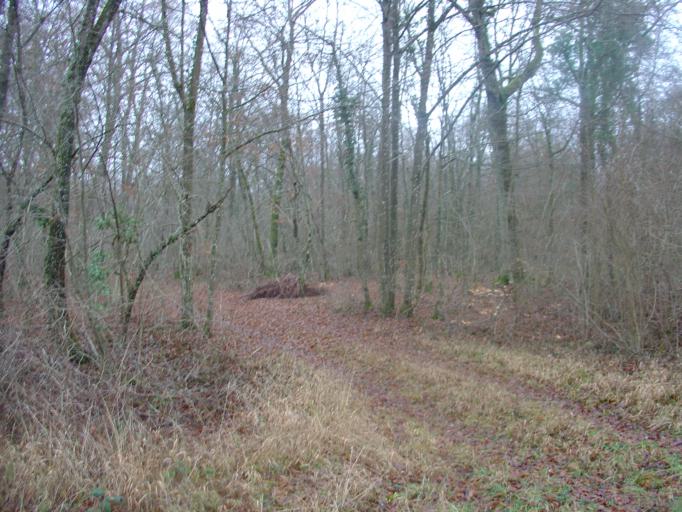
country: FR
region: Lorraine
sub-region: Departement de Meurthe-et-Moselle
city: Villey-Saint-Etienne
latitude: 48.7990
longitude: 5.9583
